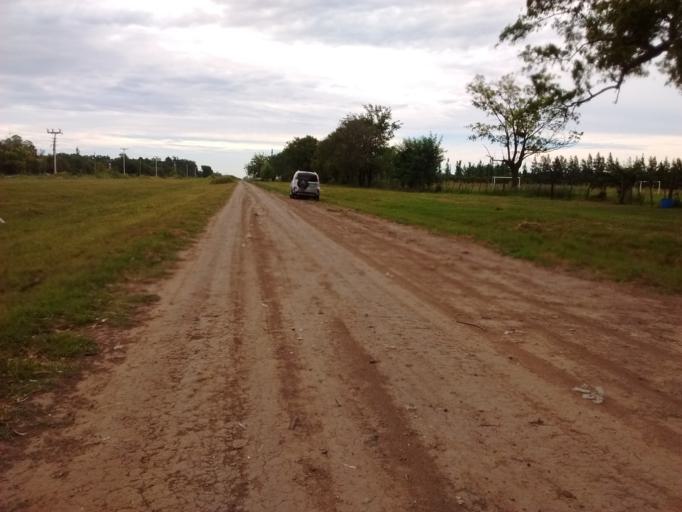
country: AR
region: Santa Fe
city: Funes
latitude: -32.9146
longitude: -60.8226
